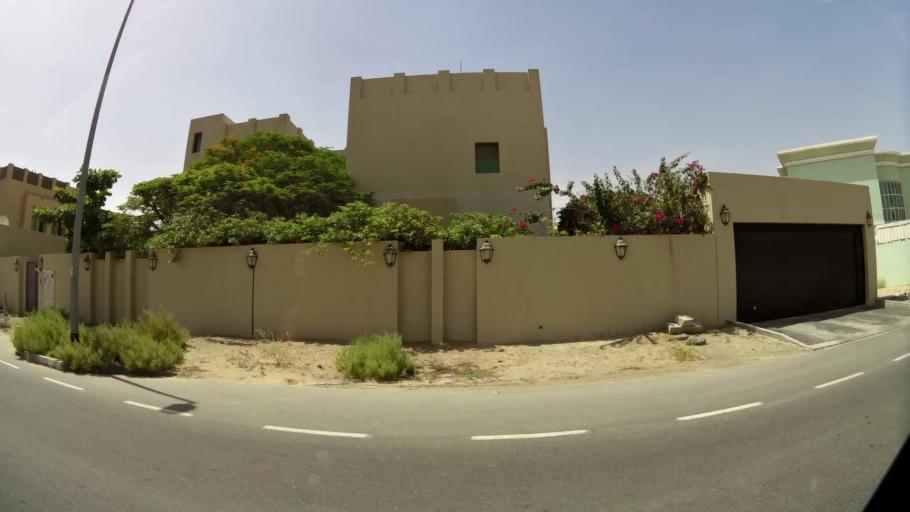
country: AE
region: Ash Shariqah
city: Sharjah
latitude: 25.1848
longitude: 55.4209
